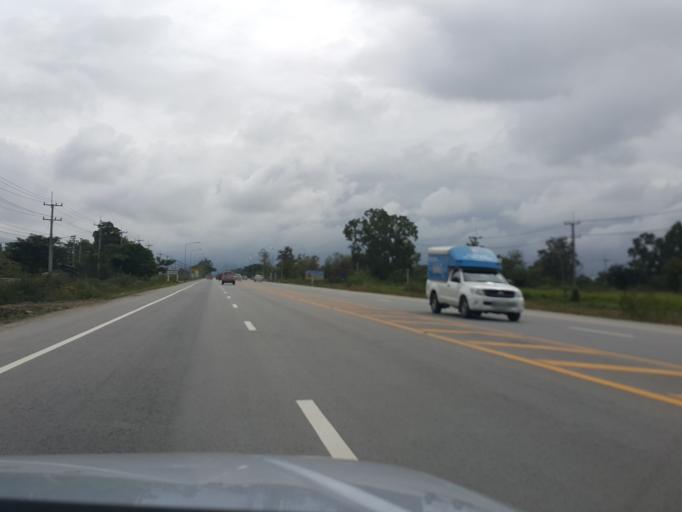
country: TH
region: Chiang Mai
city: San Kamphaeng
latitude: 18.7290
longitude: 99.0987
